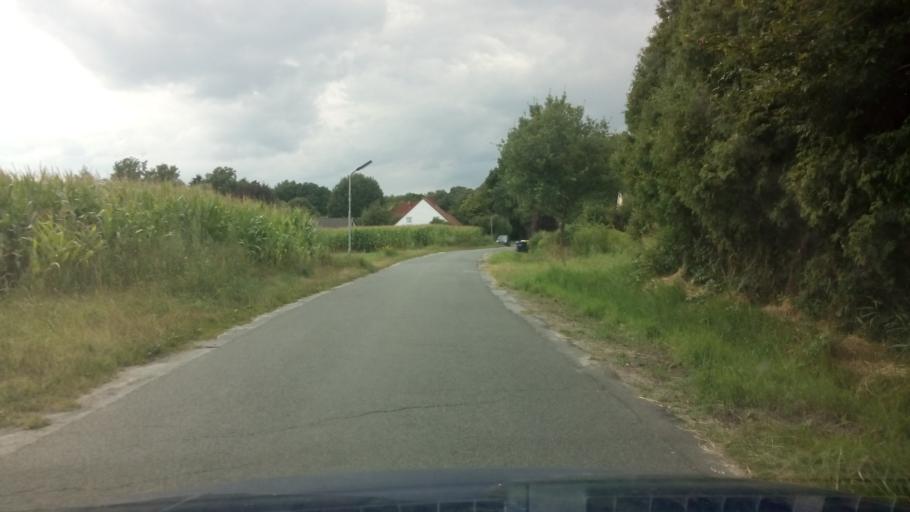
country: DE
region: Lower Saxony
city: Lilienthal
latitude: 53.1298
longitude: 8.8906
